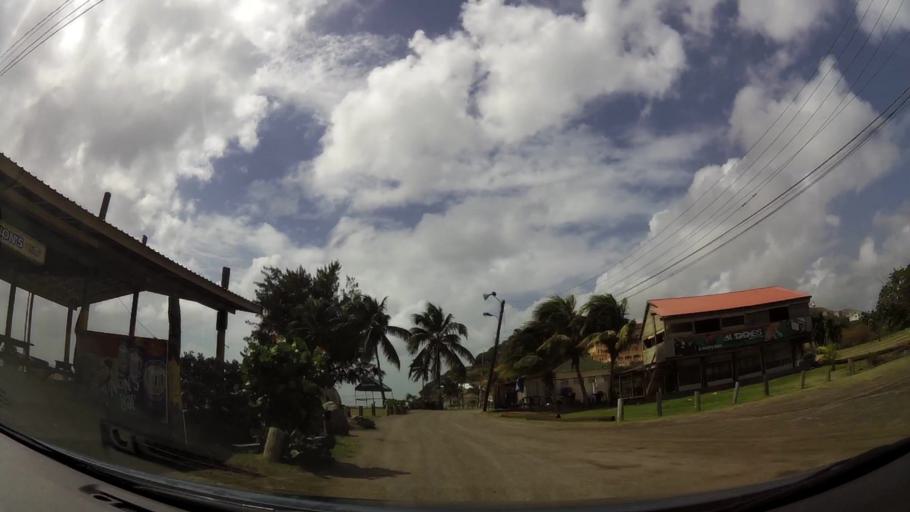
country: KN
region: Saint George Basseterre
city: Basseterre
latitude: 17.2818
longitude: -62.6896
